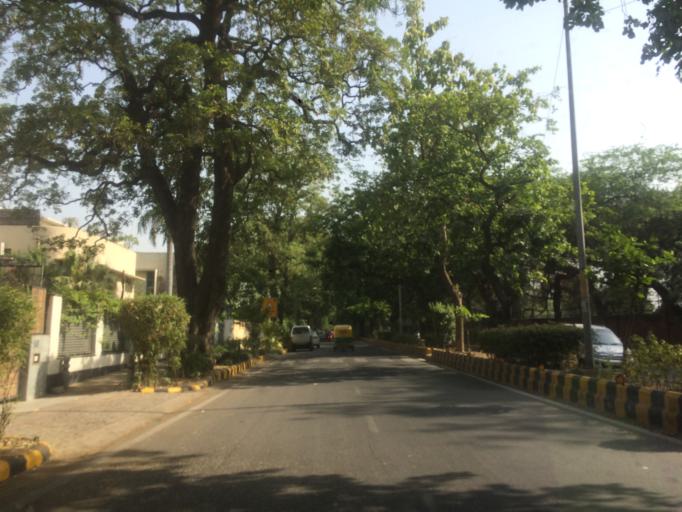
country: IN
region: NCT
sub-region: New Delhi
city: New Delhi
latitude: 28.5968
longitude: 77.2322
